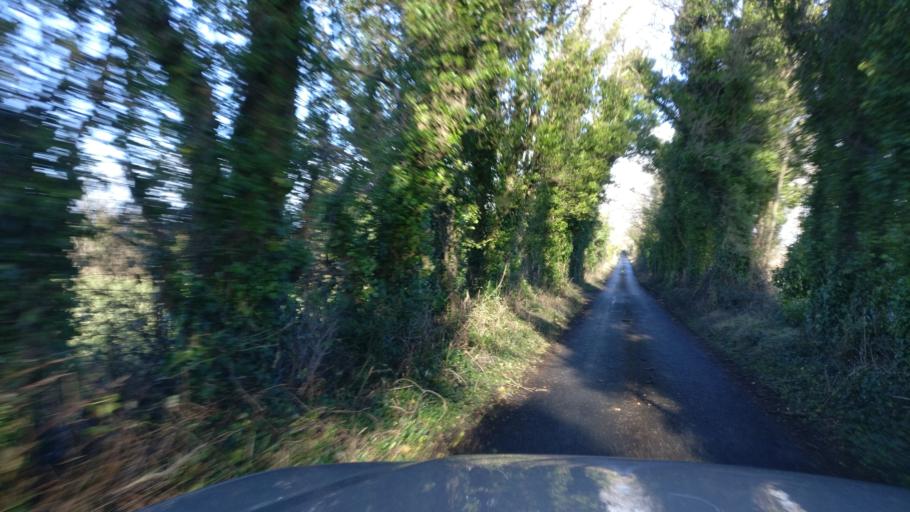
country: IE
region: Connaught
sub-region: County Galway
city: Loughrea
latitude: 53.2173
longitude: -8.6673
